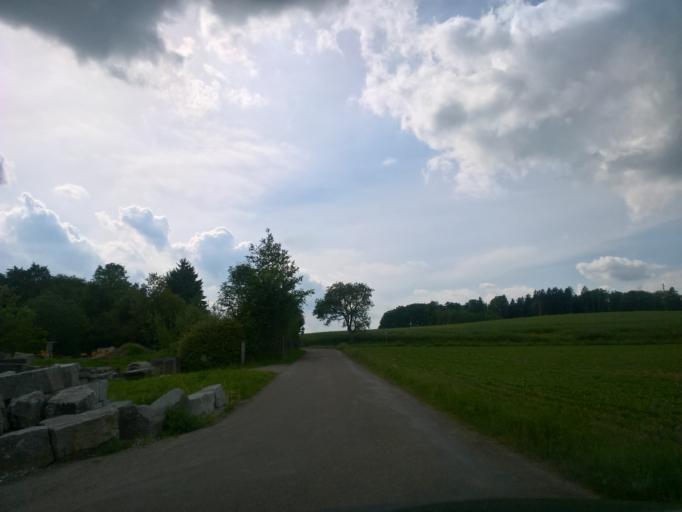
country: CH
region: Zurich
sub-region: Bezirk Buelach
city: Kloten / Freienberg (Chanzler-Chlini Chaseren)
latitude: 47.4729
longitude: 8.5878
